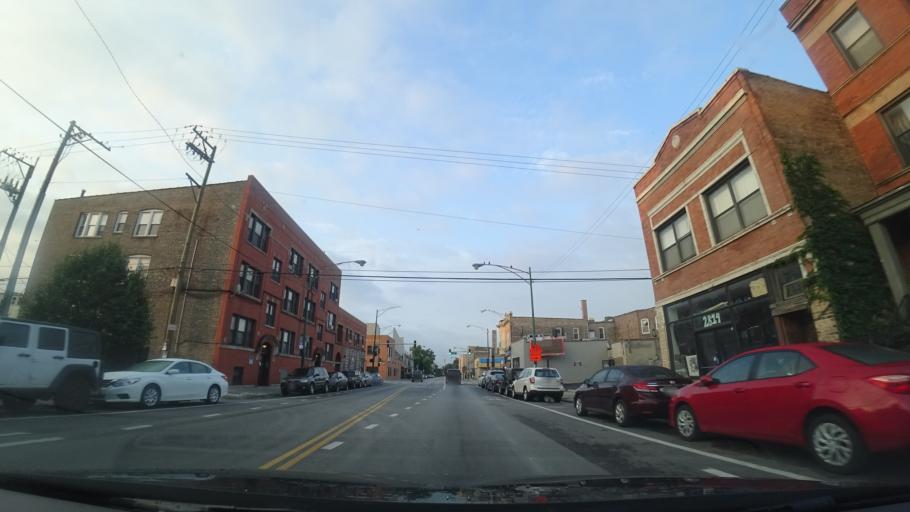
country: US
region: Illinois
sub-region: Cook County
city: Lincolnwood
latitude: 41.9326
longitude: -87.7075
